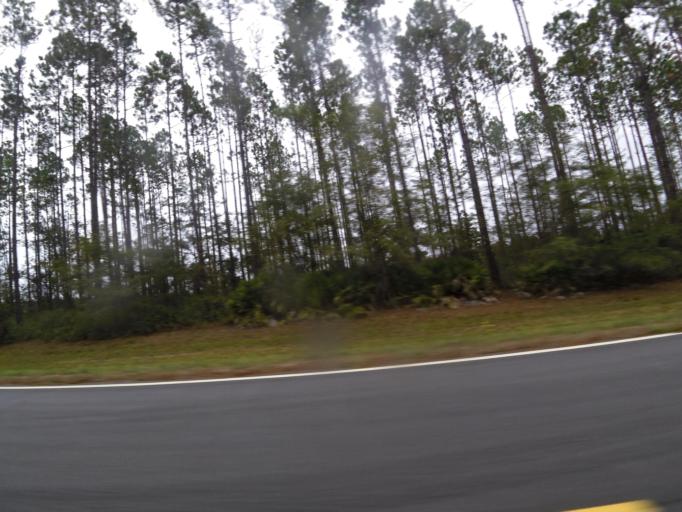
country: US
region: Georgia
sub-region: Charlton County
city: Folkston
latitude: 30.7396
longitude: -82.1080
